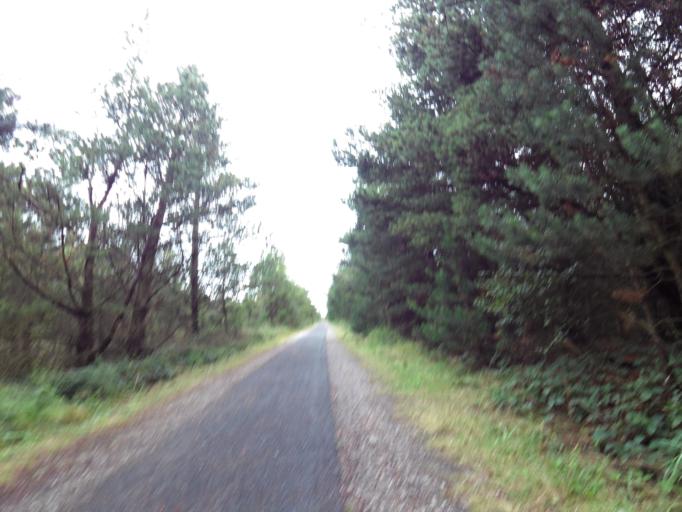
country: IE
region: Leinster
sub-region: Uibh Fhaili
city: Ferbane
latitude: 53.2162
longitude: -7.7515
